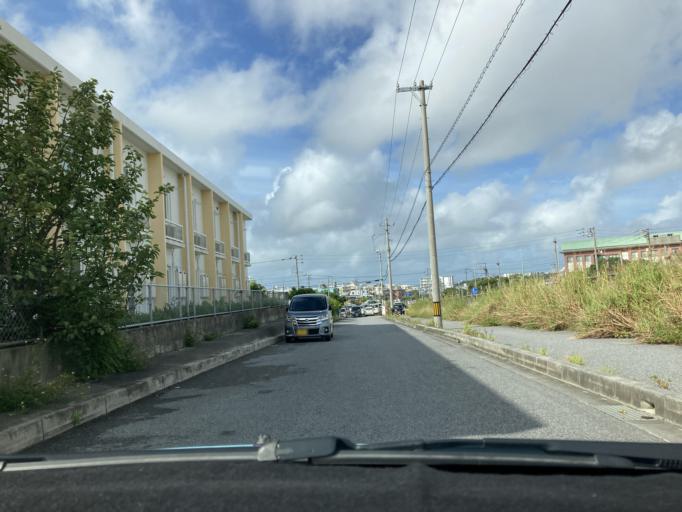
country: JP
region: Okinawa
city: Naha-shi
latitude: 26.2052
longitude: 127.7281
